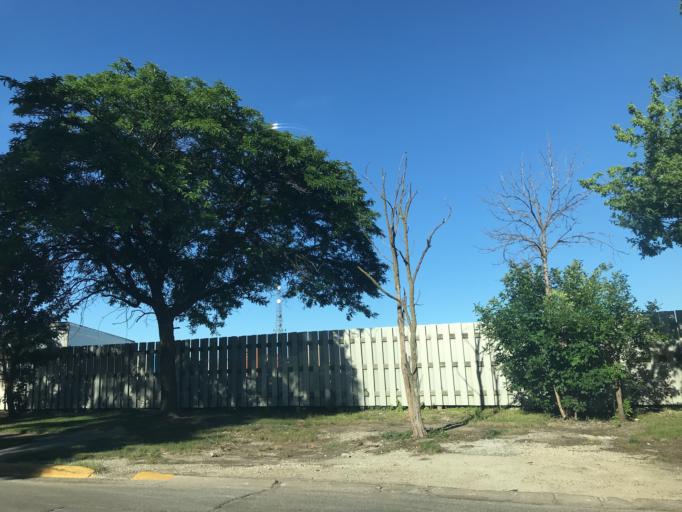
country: US
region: Illinois
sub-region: Cook County
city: Cicero
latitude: 41.8417
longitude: -87.7687
